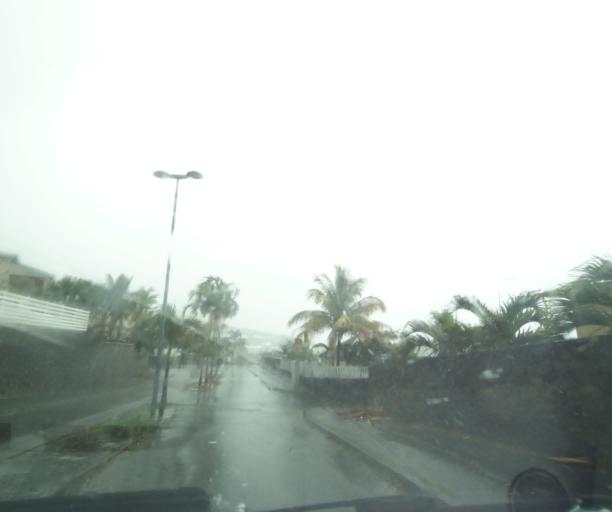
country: RE
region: Reunion
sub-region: Reunion
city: Saint-Paul
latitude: -20.9900
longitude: 55.3286
